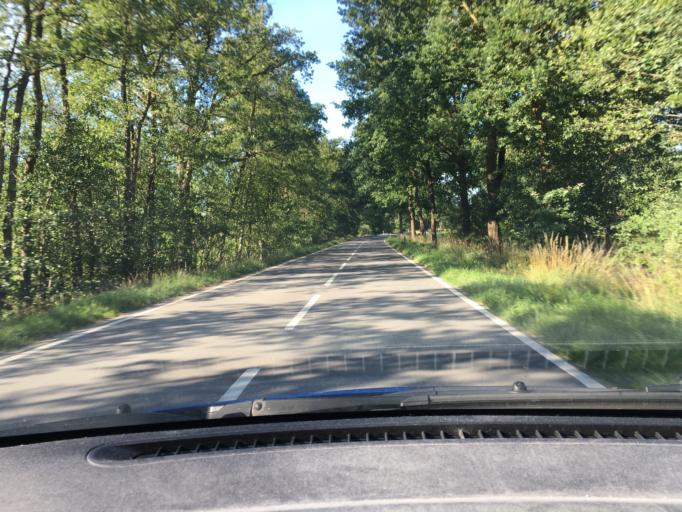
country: DE
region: Lower Saxony
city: Bleckede
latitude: 53.3275
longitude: 10.6764
